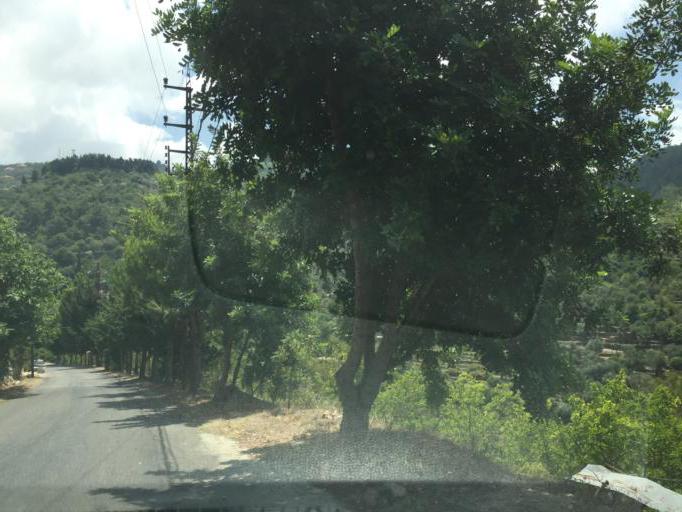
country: LB
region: Mont-Liban
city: Beit ed Dine
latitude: 33.6952
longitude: 35.5708
